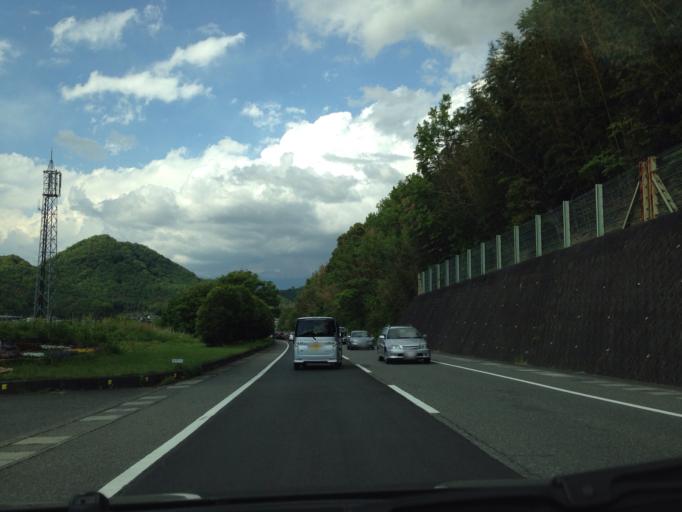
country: JP
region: Shizuoka
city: Mishima
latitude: 35.0498
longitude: 138.9227
